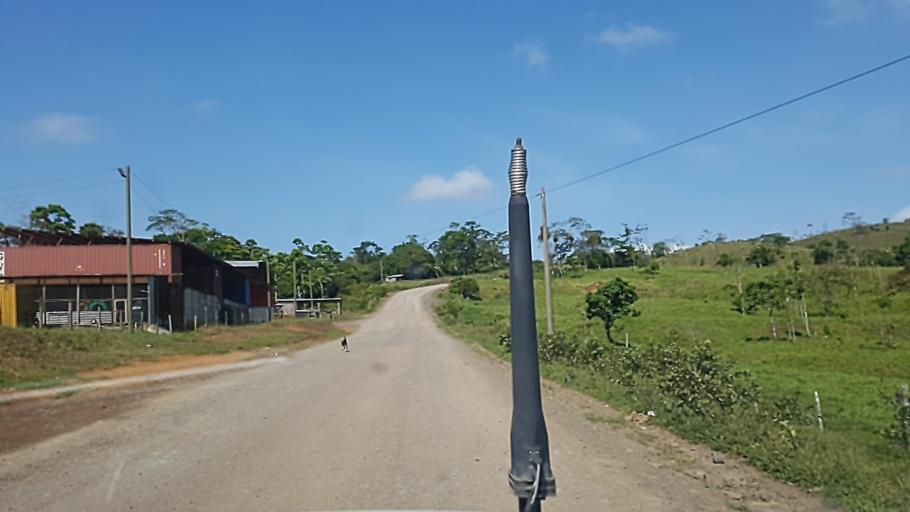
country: NI
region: Atlantico Sur
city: Nueva Guinea
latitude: 11.7891
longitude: -84.1621
